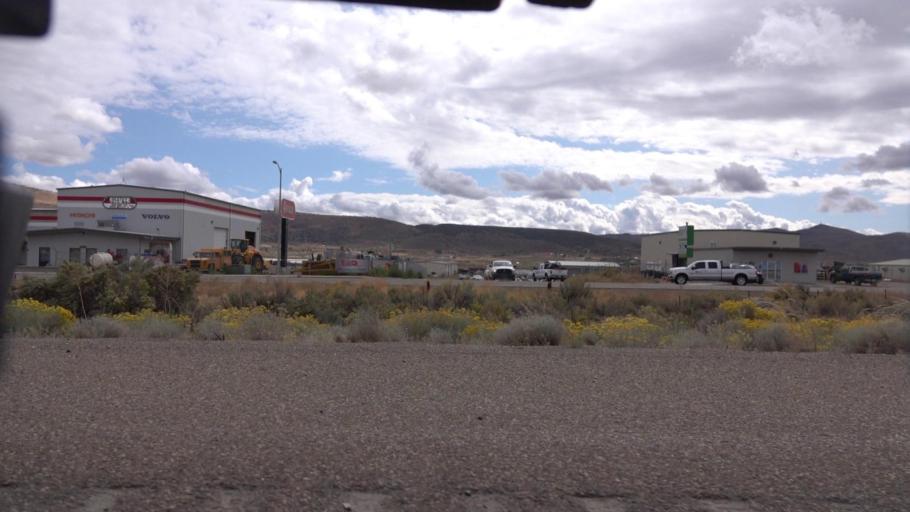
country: US
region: Nevada
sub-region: Elko County
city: Elko
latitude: 40.8689
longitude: -115.7292
